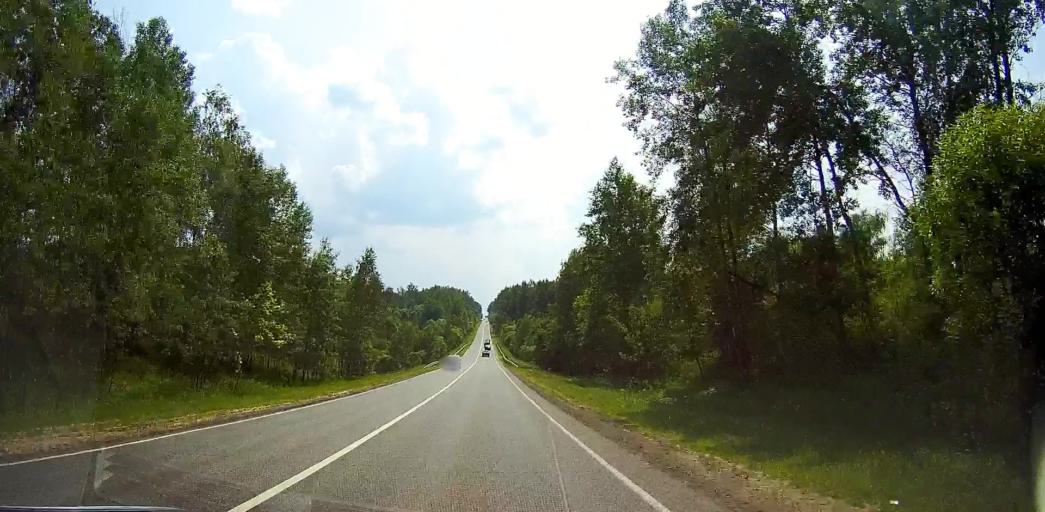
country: RU
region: Moskovskaya
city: Malino
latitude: 55.0199
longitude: 38.1745
